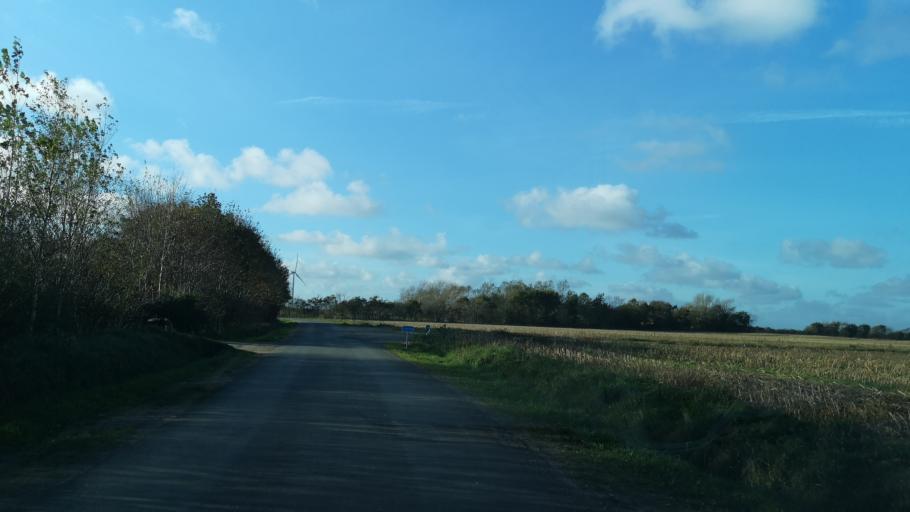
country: DK
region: Central Jutland
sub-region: Ringkobing-Skjern Kommune
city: Skjern
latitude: 55.8579
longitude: 8.3461
